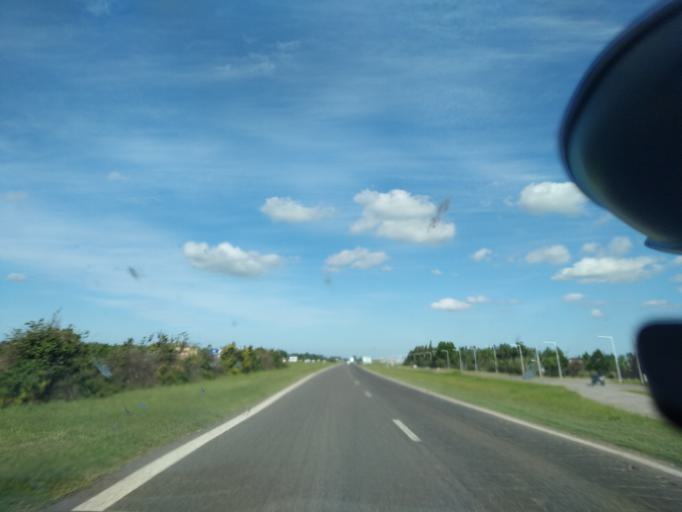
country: AR
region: Santa Fe
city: Roldan
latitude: -32.9283
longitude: -60.8858
